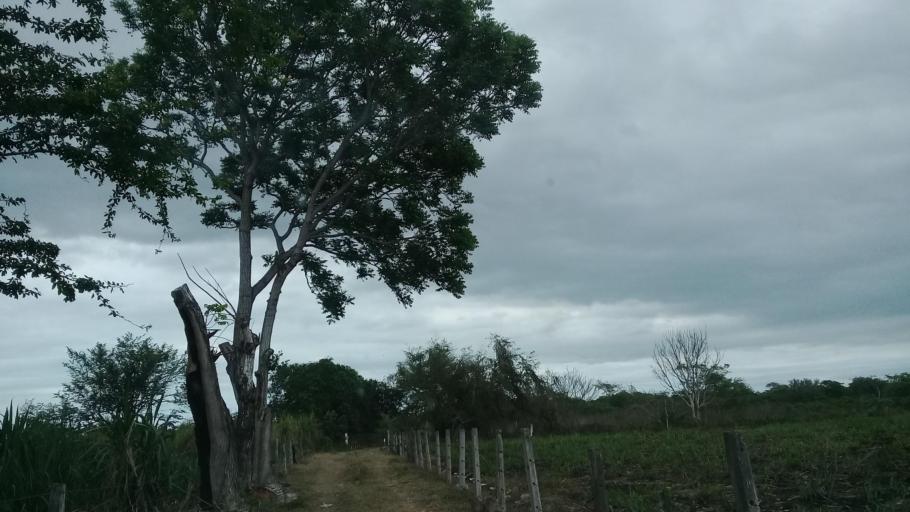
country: MX
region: Veracruz
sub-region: Puente Nacional
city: Cabezas
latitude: 19.3739
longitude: -96.3626
